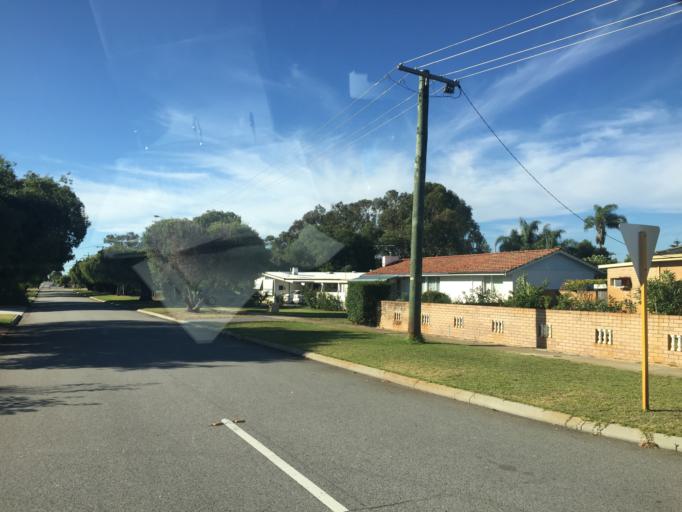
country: AU
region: Western Australia
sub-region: Belmont
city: Rivervale
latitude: -31.9647
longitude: 115.9239
